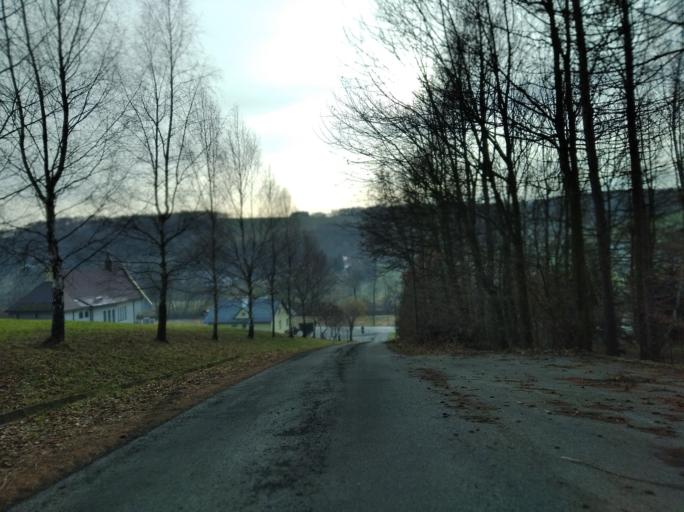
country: PL
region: Subcarpathian Voivodeship
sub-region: Powiat strzyzowski
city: Czudec
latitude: 49.9260
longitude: 21.7998
